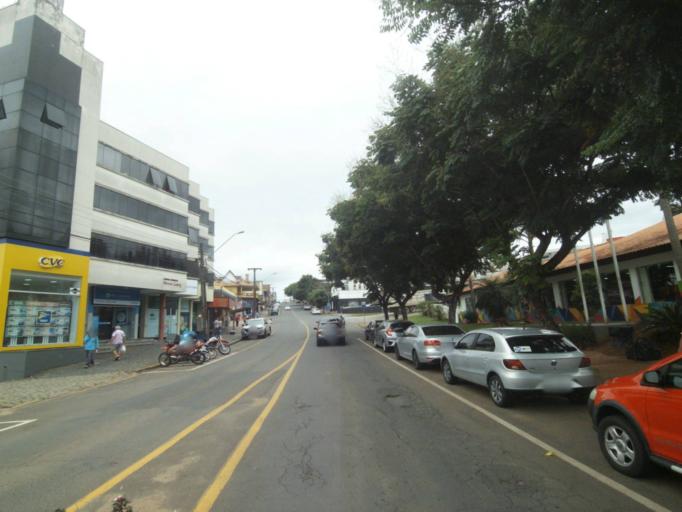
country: BR
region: Parana
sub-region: Telemaco Borba
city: Telemaco Borba
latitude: -24.3230
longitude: -50.6200
